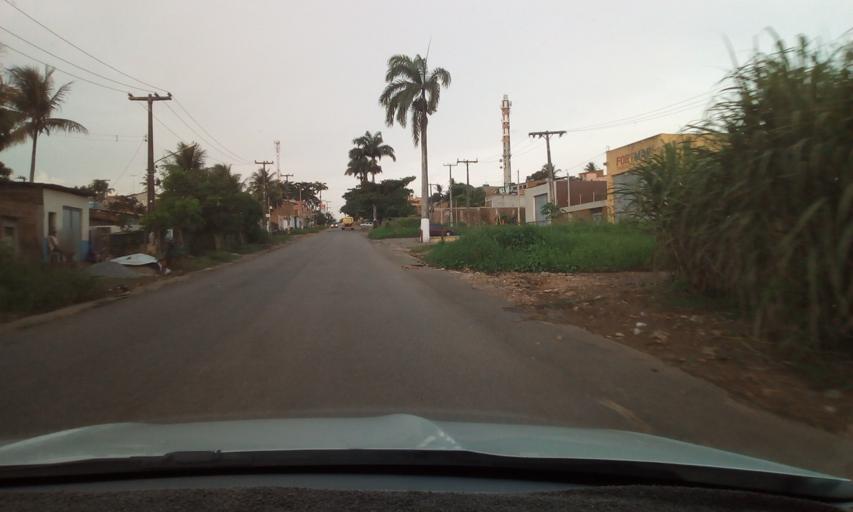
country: BR
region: Pernambuco
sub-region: Vicencia
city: Vicencia
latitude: -7.6002
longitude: -35.2361
